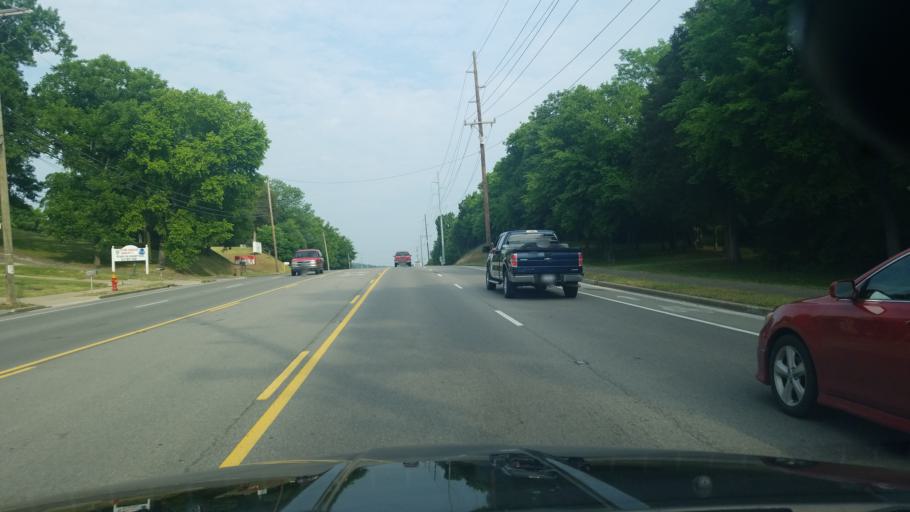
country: US
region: Tennessee
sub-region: Davidson County
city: Goodlettsville
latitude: 36.2684
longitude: -86.7513
